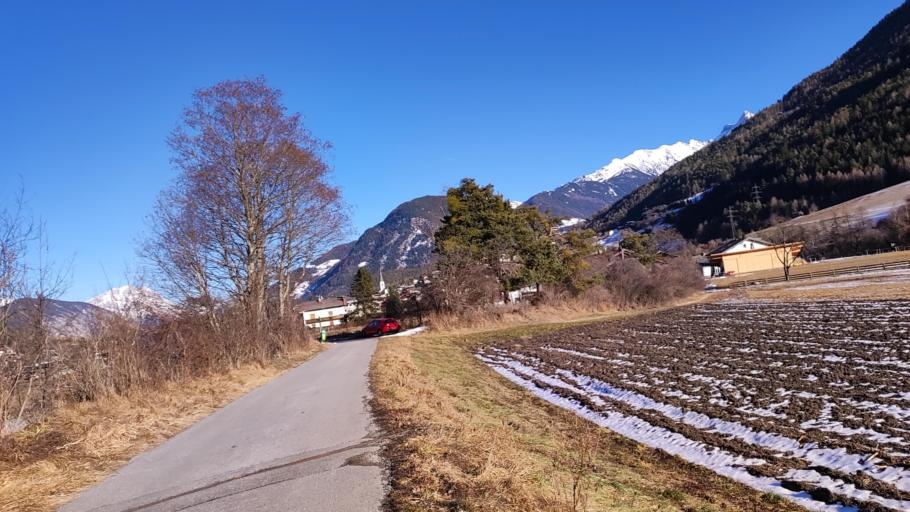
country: AT
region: Tyrol
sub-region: Politischer Bezirk Imst
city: Roppen
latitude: 47.2151
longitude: 10.8076
